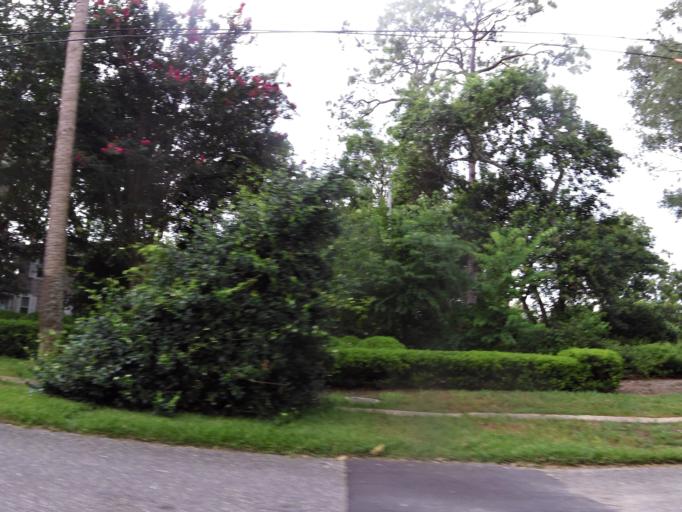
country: US
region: Florida
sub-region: Duval County
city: Jacksonville
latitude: 30.2904
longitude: -81.7057
